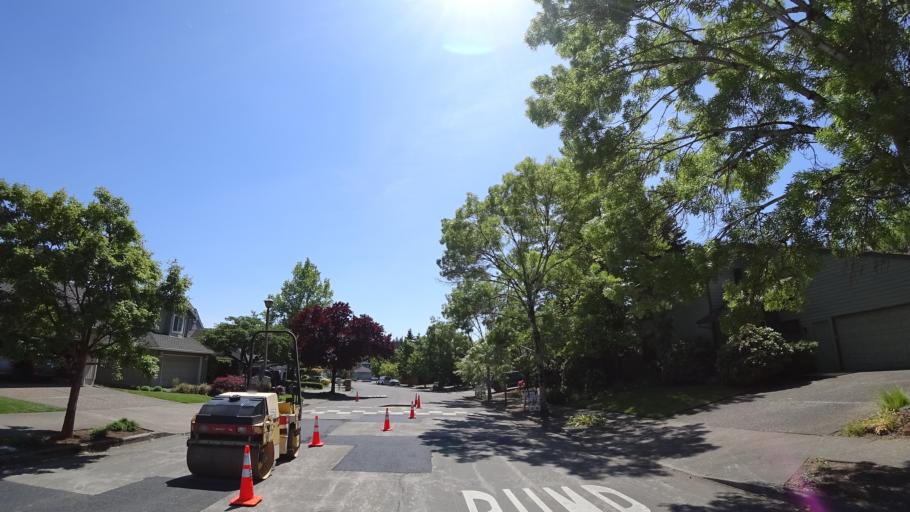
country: US
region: Oregon
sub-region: Washington County
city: Tigard
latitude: 45.4415
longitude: -122.8086
